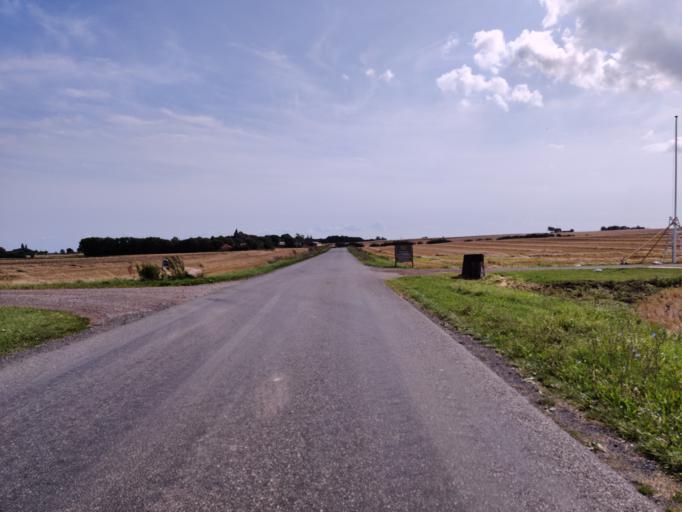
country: DK
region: Zealand
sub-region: Guldborgsund Kommune
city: Nykobing Falster
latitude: 54.6399
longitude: 11.8970
